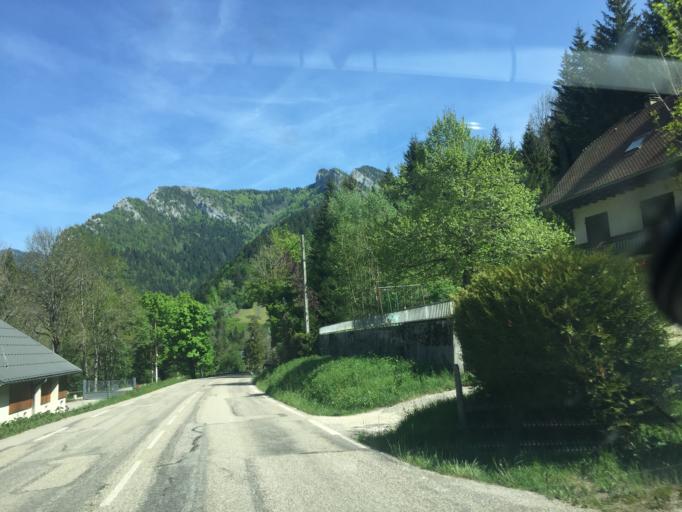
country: FR
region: Rhone-Alpes
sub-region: Departement de l'Isere
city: Le Sappey-en-Chartreuse
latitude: 45.3358
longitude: 5.8073
